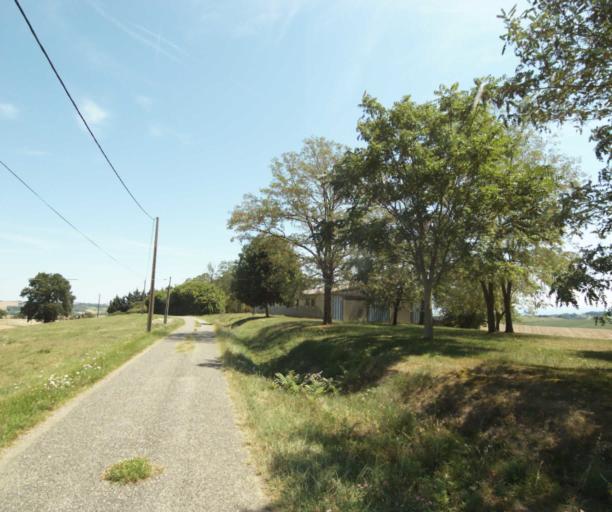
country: FR
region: Midi-Pyrenees
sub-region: Departement de l'Ariege
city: Lezat-sur-Leze
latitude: 43.2651
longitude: 1.3171
